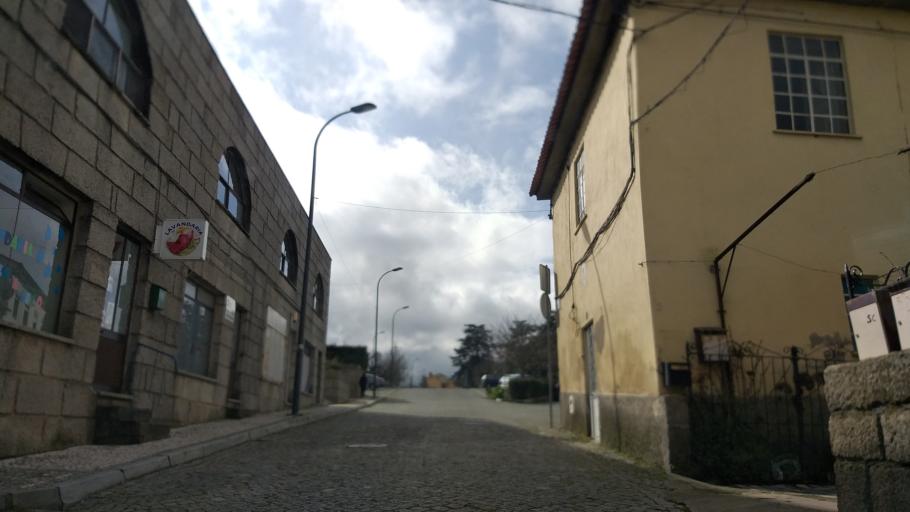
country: PT
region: Guarda
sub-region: Celorico da Beira
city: Celorico da Beira
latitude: 40.6351
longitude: -7.3925
